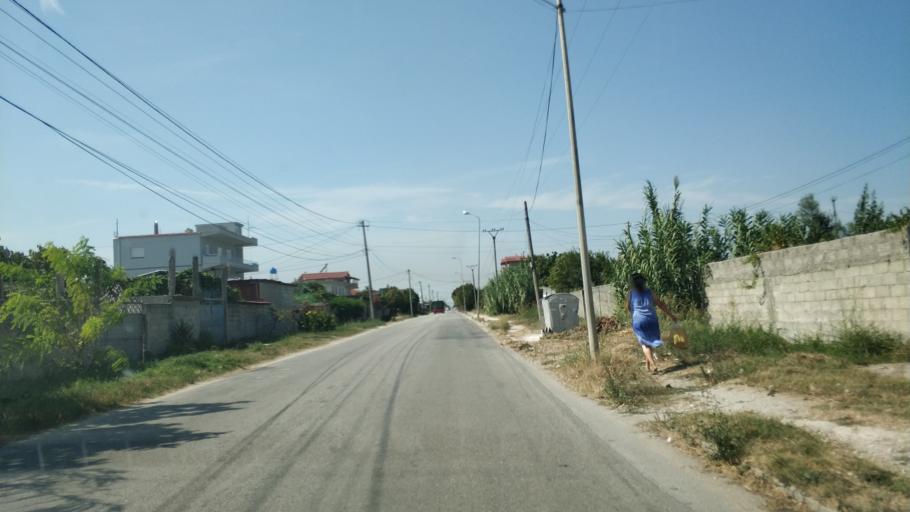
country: AL
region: Fier
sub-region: Rrethi i Fierit
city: Dermenas
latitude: 40.7439
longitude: 19.4978
